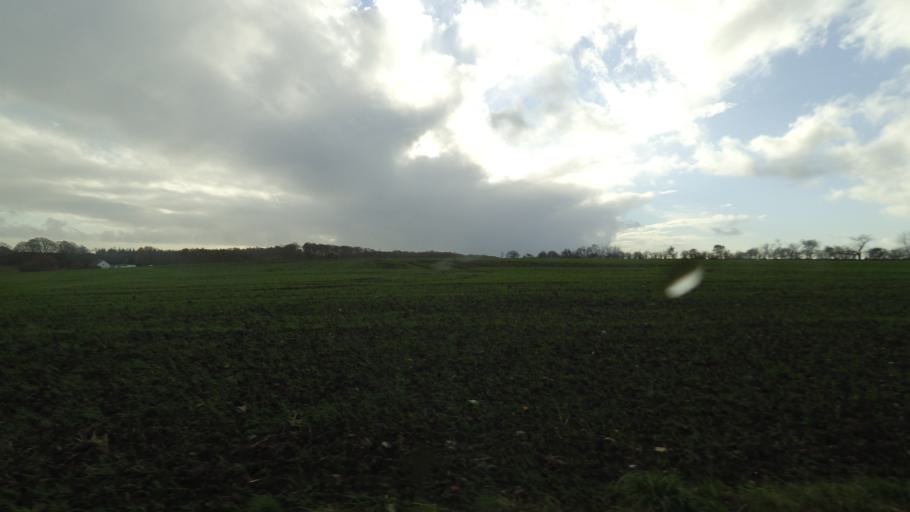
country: DK
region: Central Jutland
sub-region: Odder Kommune
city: Odder
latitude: 55.9057
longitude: 10.2009
